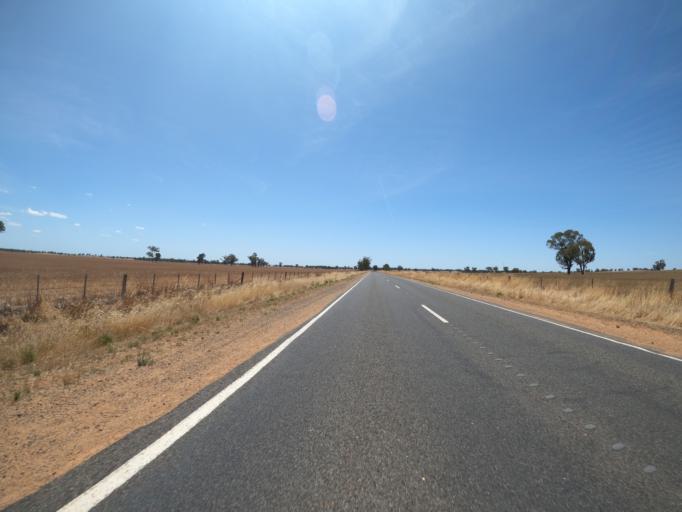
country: AU
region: Victoria
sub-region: Moira
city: Yarrawonga
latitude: -36.1543
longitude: 145.9673
